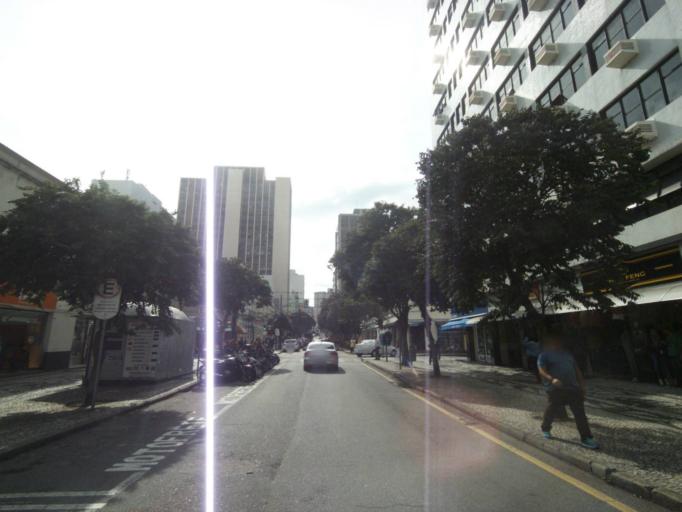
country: BR
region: Parana
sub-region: Curitiba
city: Curitiba
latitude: -25.4324
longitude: -49.2682
